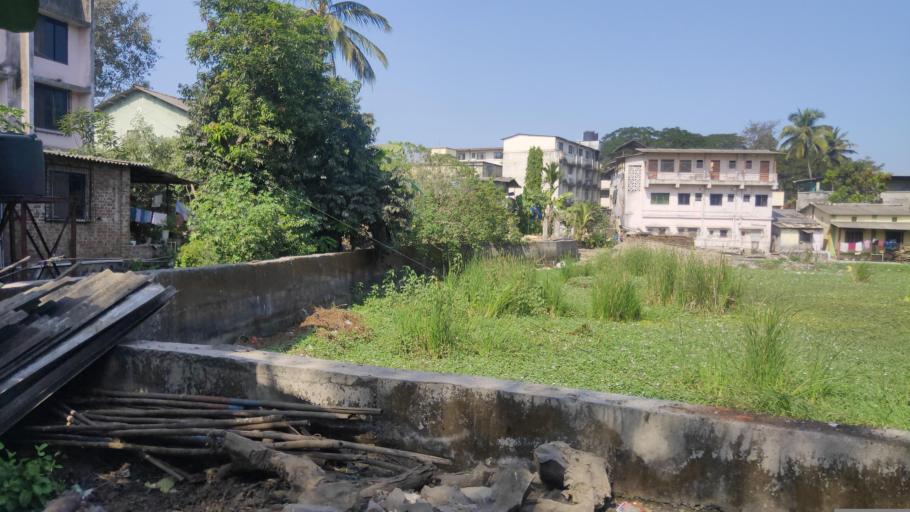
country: IN
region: Maharashtra
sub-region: Thane
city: Vada
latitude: 19.5005
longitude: 73.0142
